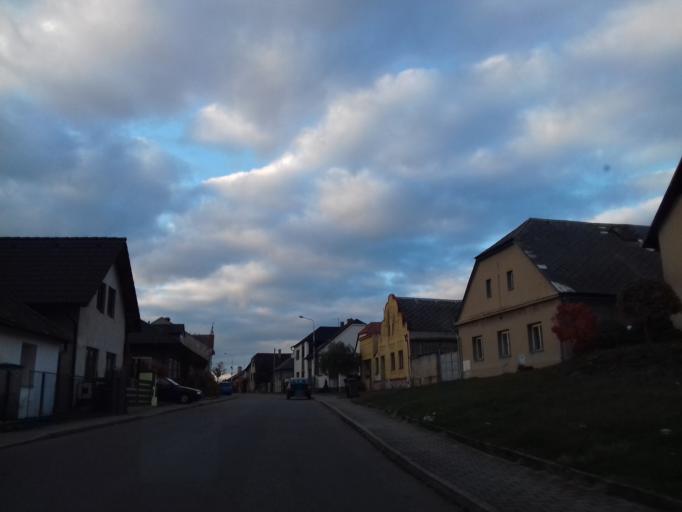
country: CZ
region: Pardubicky
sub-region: Okres Chrudim
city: Skutec
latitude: 49.8408
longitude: 16.0033
